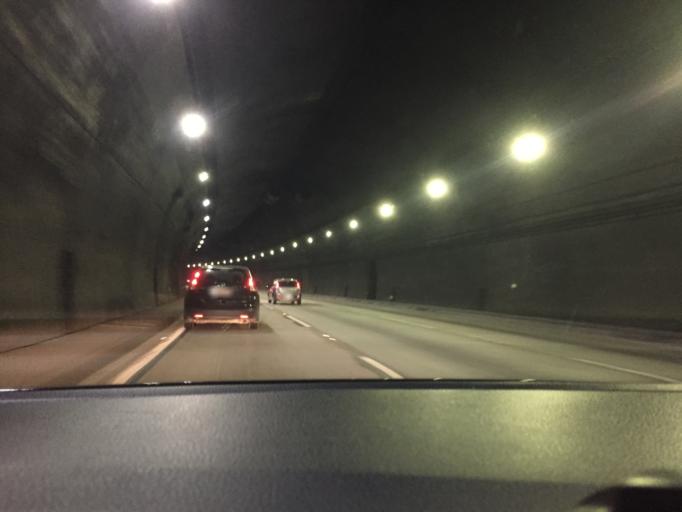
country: BR
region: Sao Paulo
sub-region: Cubatao
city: Cubatao
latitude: -23.8891
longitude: -46.5027
